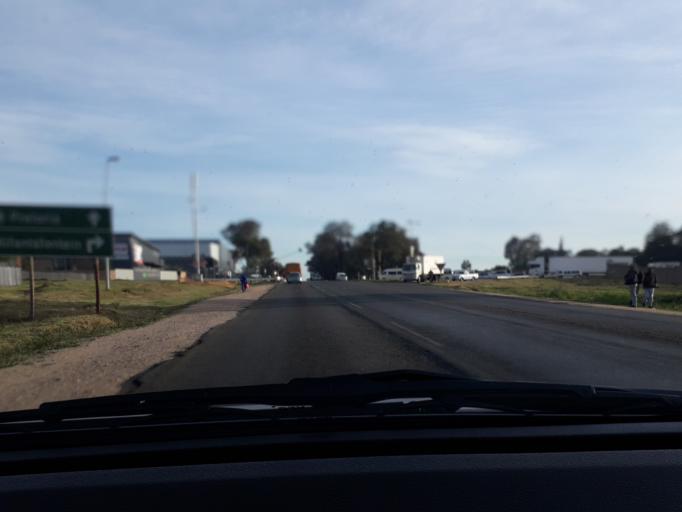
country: ZA
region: Gauteng
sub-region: City of Johannesburg Metropolitan Municipality
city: Midrand
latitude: -25.9443
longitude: 28.1437
